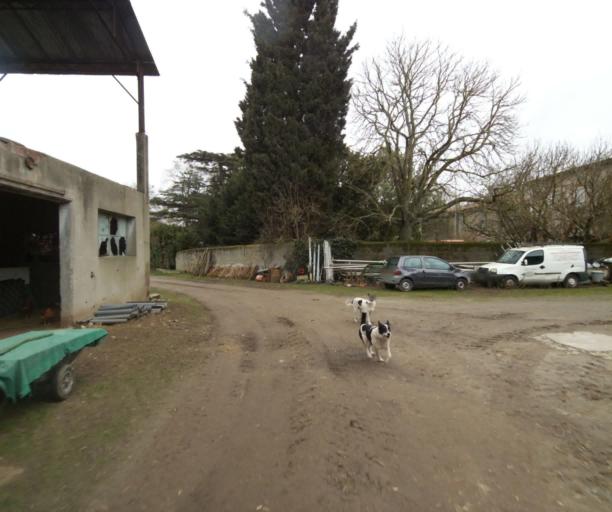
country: FR
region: Midi-Pyrenees
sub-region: Departement de l'Ariege
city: Saverdun
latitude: 43.1932
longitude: 1.6045
